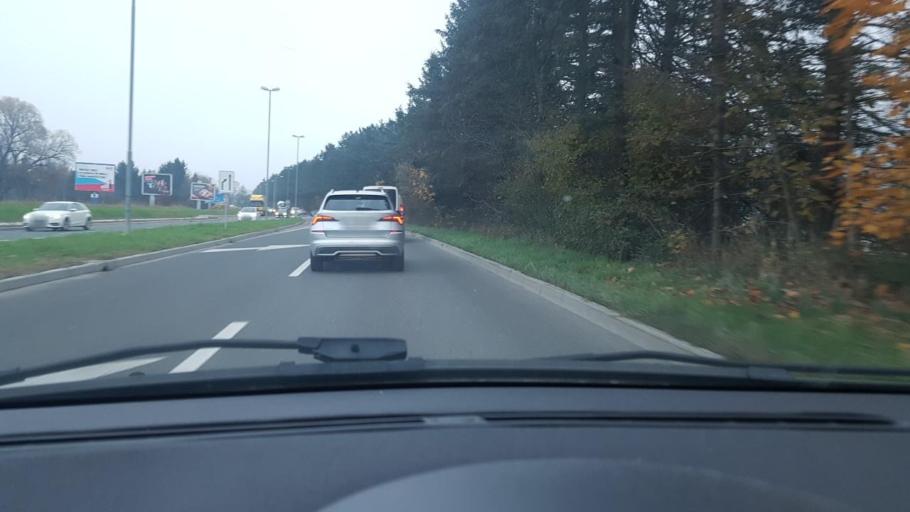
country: SI
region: Celje
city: Celje
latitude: 46.2381
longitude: 15.2305
